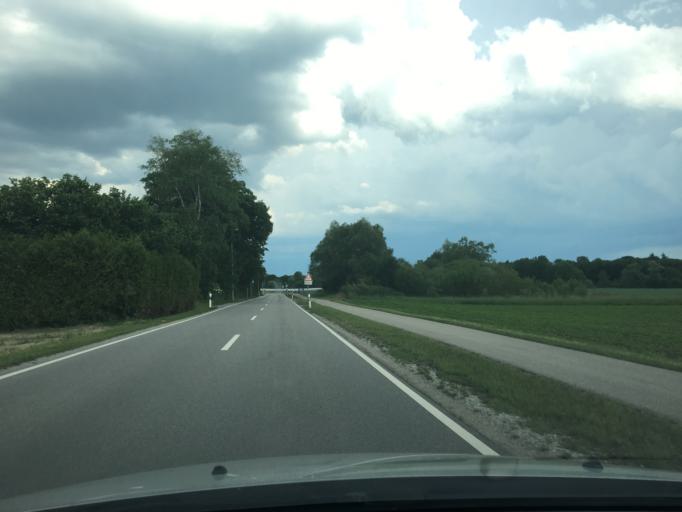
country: DE
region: Bavaria
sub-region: Upper Bavaria
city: Haimhausen
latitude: 48.3219
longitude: 11.5374
